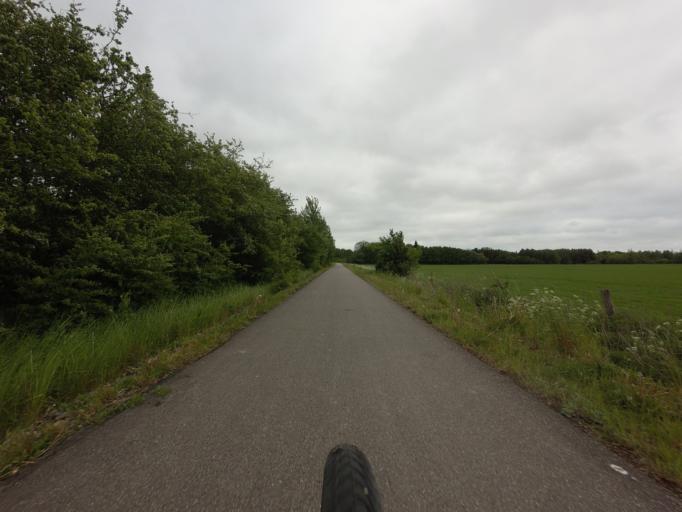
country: DK
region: Zealand
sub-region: Slagelse Kommune
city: Slagelse
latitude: 55.3020
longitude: 11.4153
